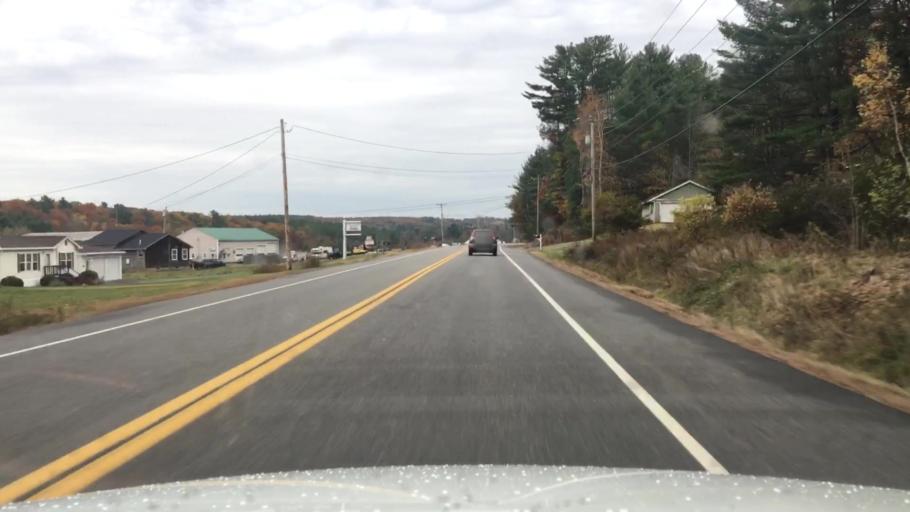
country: US
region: Maine
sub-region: Kennebec County
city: Pittston
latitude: 44.2059
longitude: -69.7540
